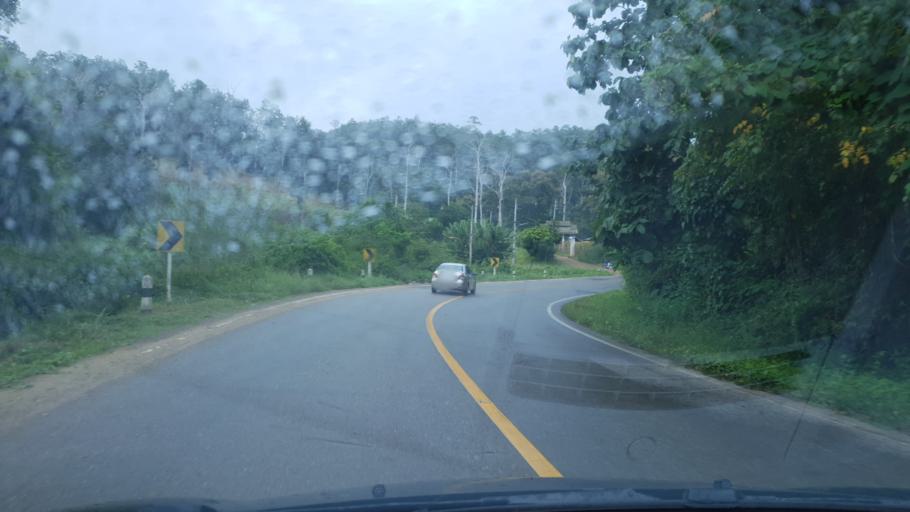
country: TH
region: Mae Hong Son
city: Khun Yuam
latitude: 18.6958
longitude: 97.9209
